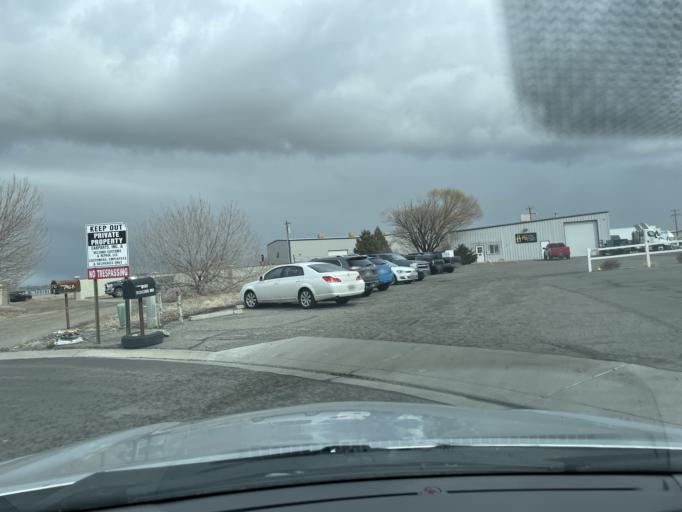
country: US
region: Colorado
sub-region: Mesa County
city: Redlands
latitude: 39.1091
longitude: -108.6298
